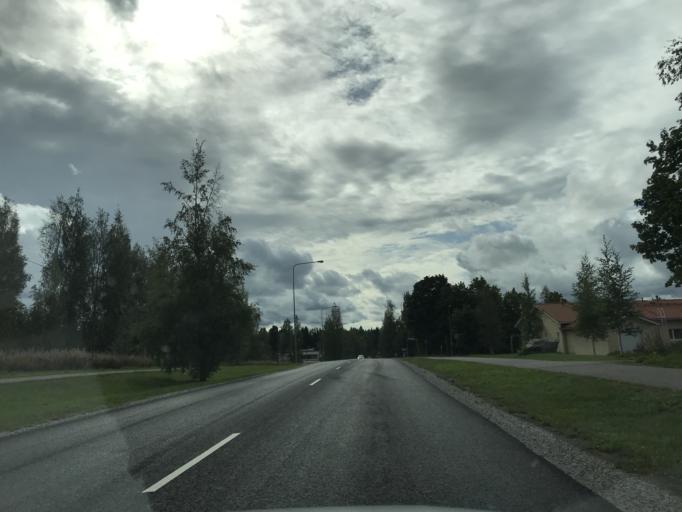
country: FI
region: Paijanne Tavastia
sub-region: Lahti
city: Lahti
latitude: 61.0068
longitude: 25.7789
